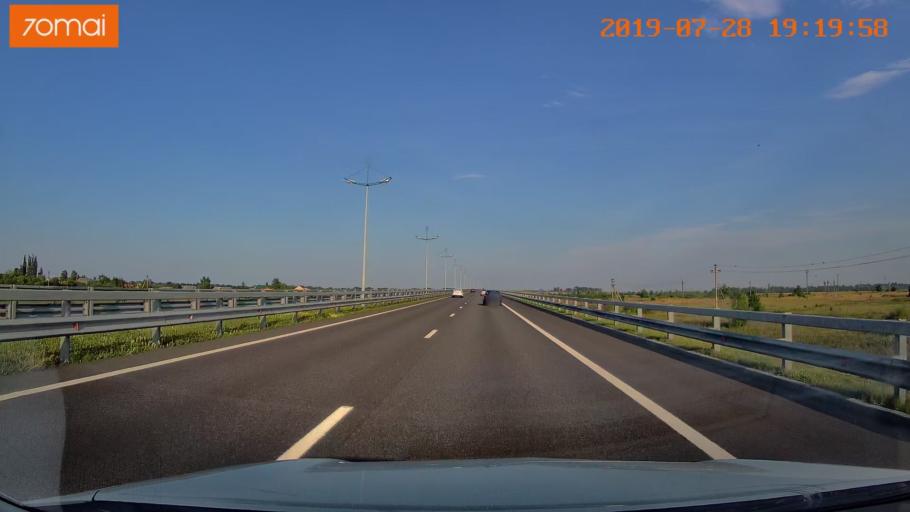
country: RU
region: Kaliningrad
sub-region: Zelenogradskiy Rayon
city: Zelenogradsk
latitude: 54.9184
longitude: 20.4736
